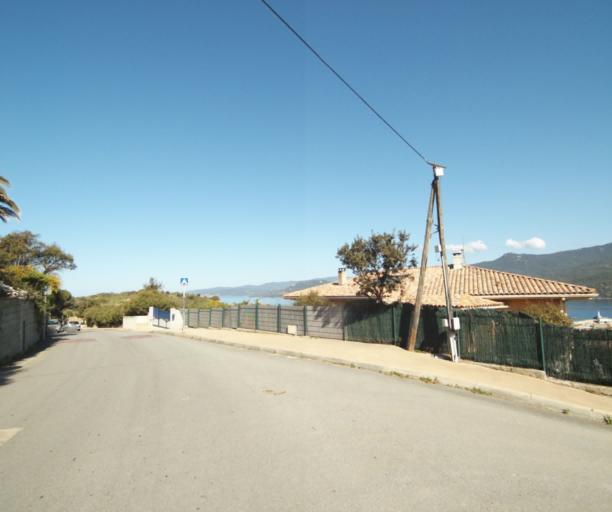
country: FR
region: Corsica
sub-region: Departement de la Corse-du-Sud
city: Propriano
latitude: 41.6698
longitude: 8.8991
